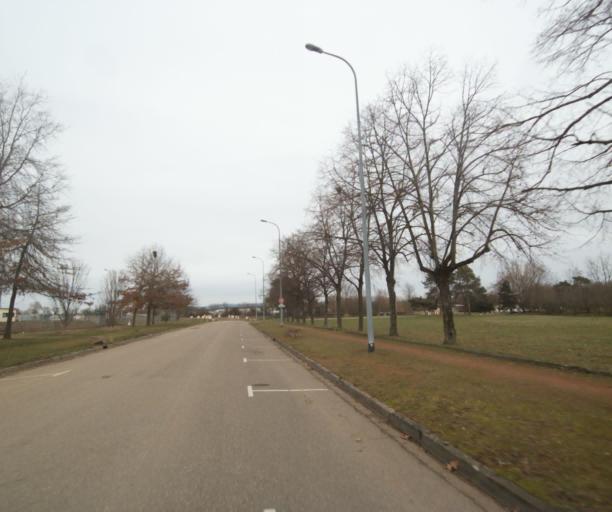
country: FR
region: Rhone-Alpes
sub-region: Departement de la Loire
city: Le Coteau
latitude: 46.0612
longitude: 4.0920
